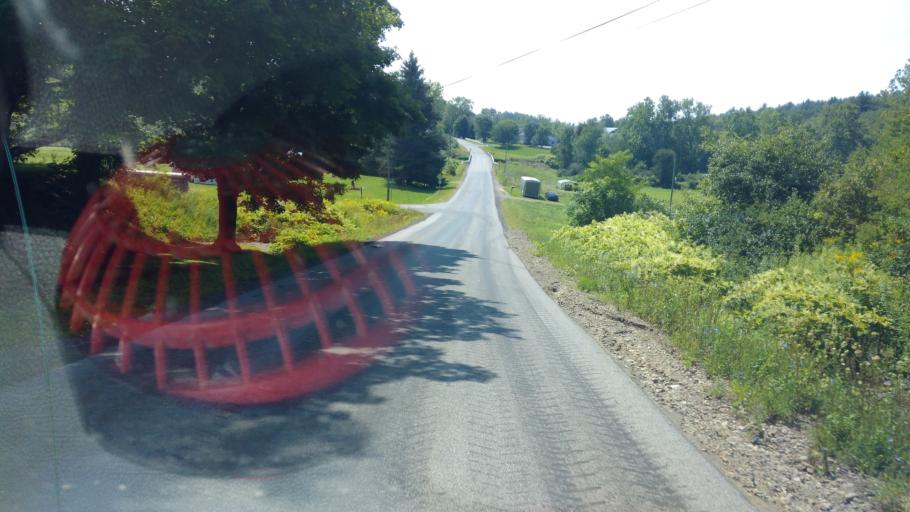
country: US
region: New York
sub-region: Allegany County
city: Belmont
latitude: 42.3274
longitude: -78.0372
